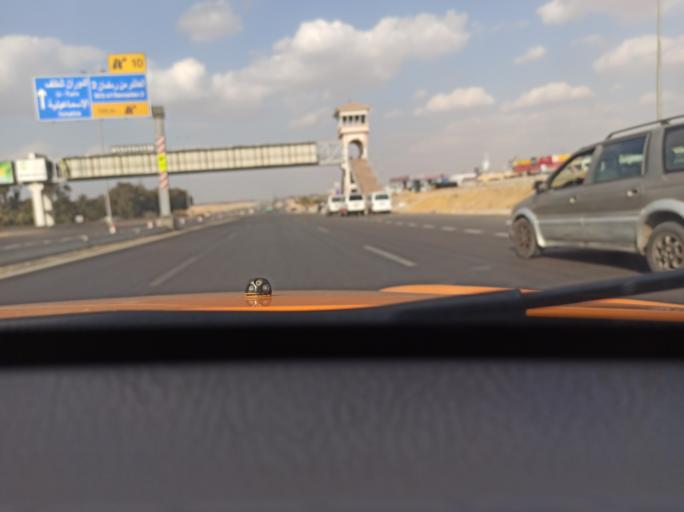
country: EG
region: Eastern Province
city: Bilbays
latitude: 30.2437
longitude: 31.7247
